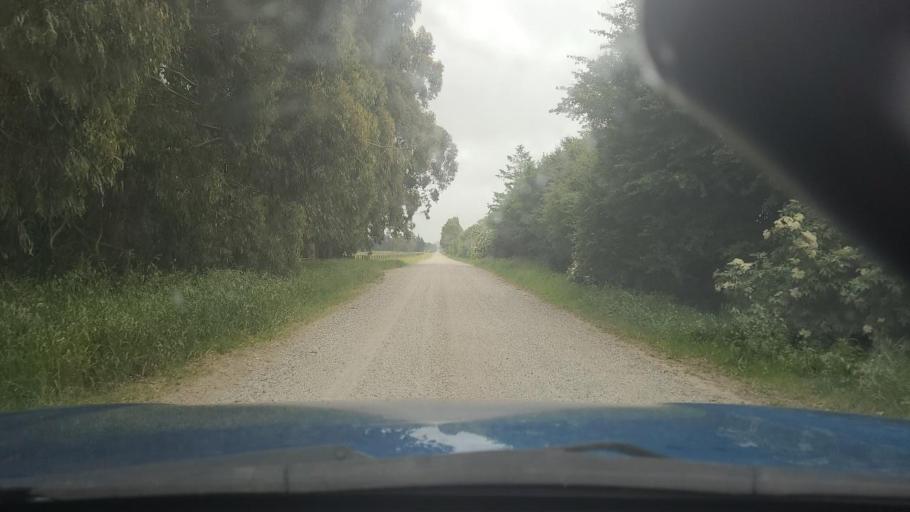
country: NZ
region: Southland
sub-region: Gore District
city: Gore
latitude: -46.3300
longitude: 168.7843
